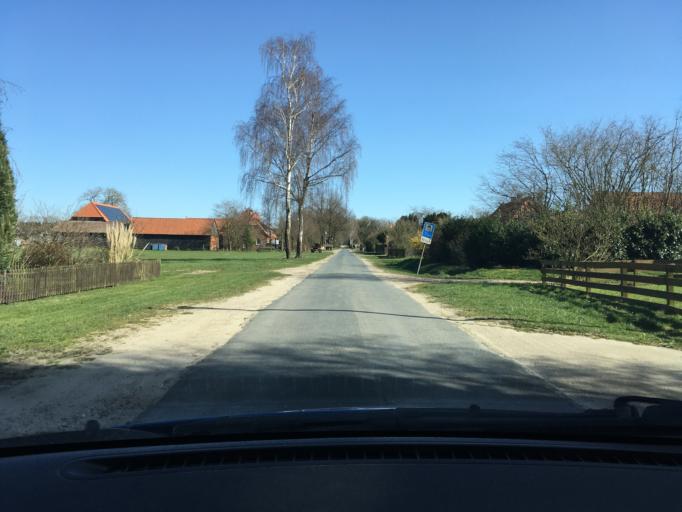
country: DE
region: Lower Saxony
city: Ebstorf
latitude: 53.0252
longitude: 10.4388
